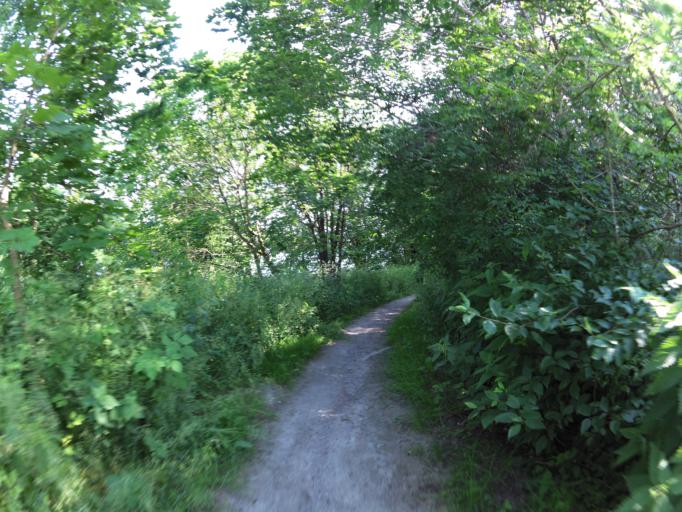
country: NO
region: Ostfold
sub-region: Sarpsborg
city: Sarpsborg
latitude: 59.2587
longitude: 11.0190
